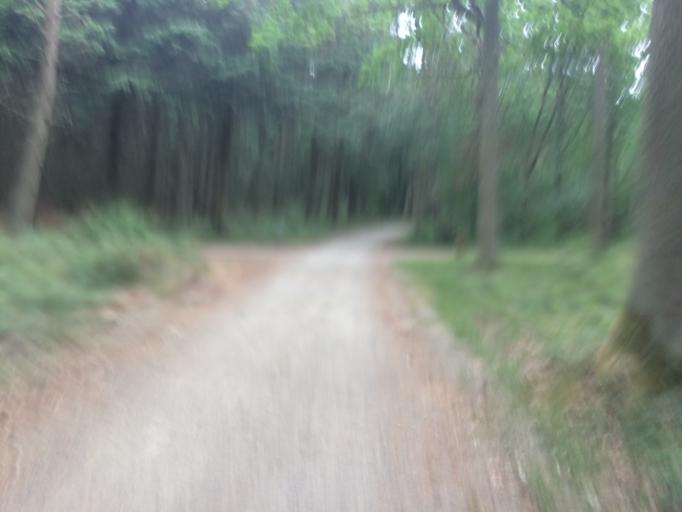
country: DK
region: Capital Region
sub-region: Bornholm Kommune
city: Ronne
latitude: 55.1250
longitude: 14.7107
